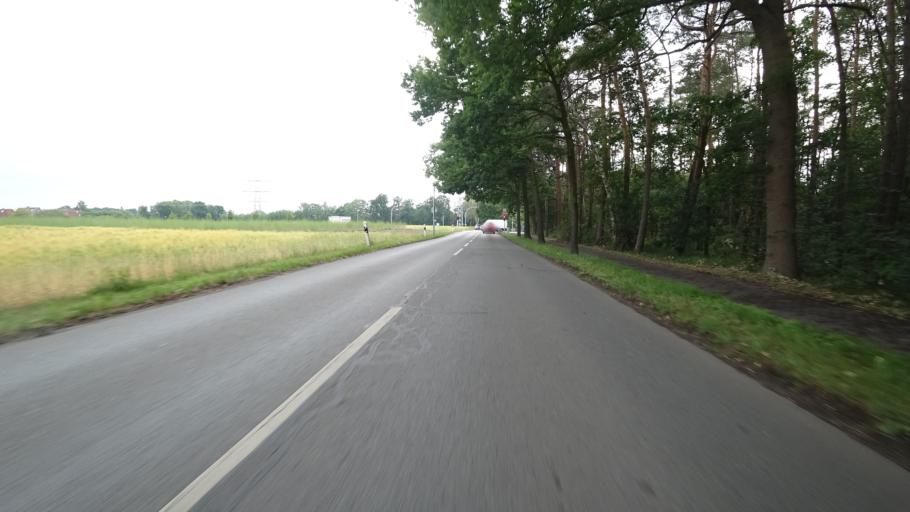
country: DE
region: North Rhine-Westphalia
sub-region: Regierungsbezirk Detmold
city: Guetersloh
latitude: 51.9336
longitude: 8.3803
